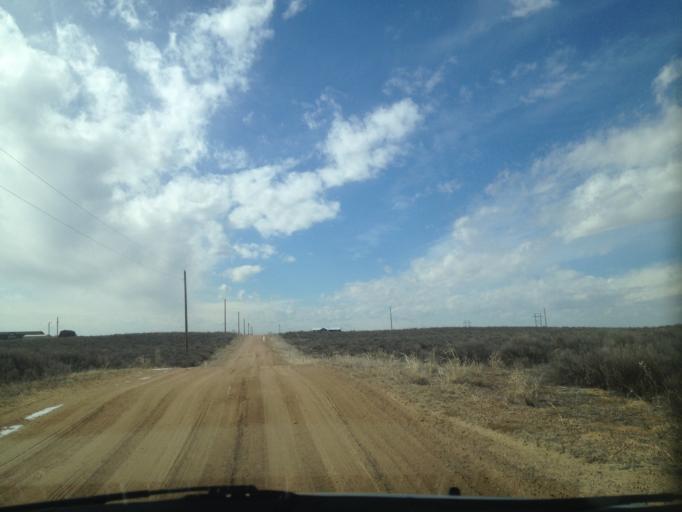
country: US
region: Colorado
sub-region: Weld County
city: Keenesburg
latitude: 40.2820
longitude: -104.2563
